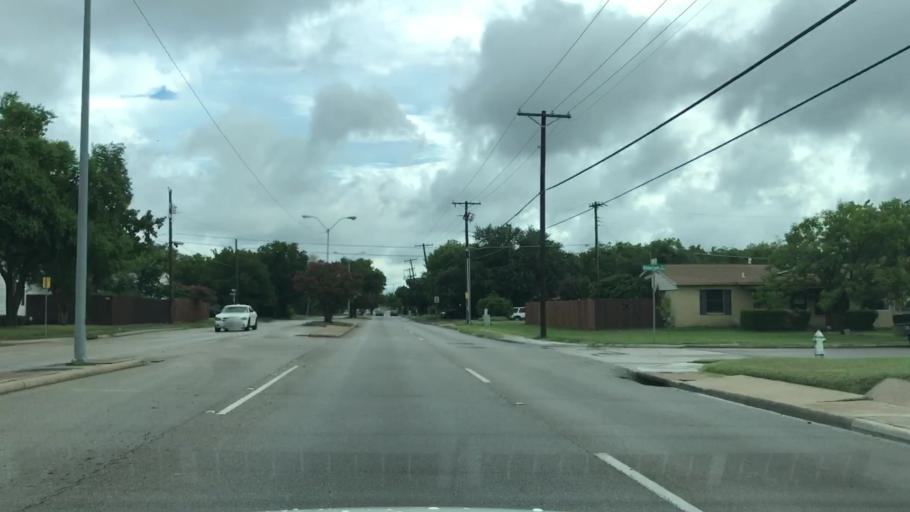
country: US
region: Texas
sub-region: Dallas County
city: Irving
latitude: 32.8466
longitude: -96.9765
